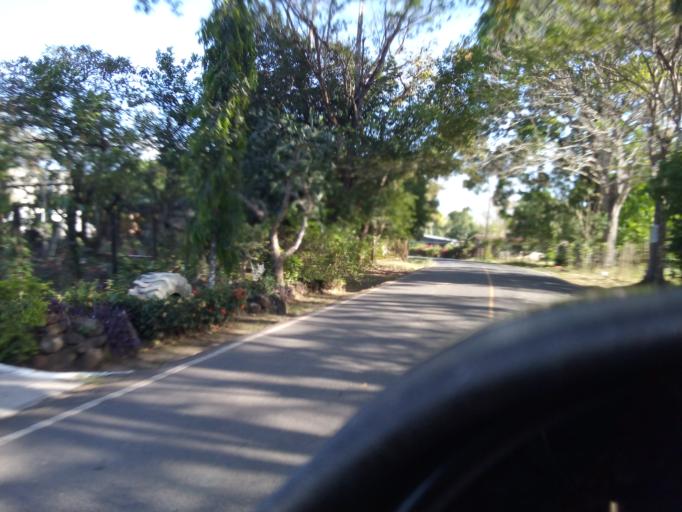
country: PA
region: Veraguas
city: Atalaya
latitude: 8.0387
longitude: -80.9241
